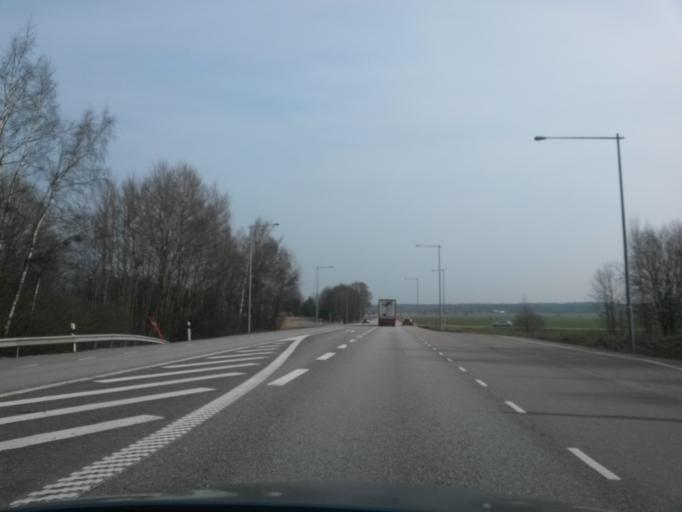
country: SE
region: Vaestra Goetaland
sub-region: Mariestads Kommun
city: Mariestad
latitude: 58.7368
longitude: 13.9293
